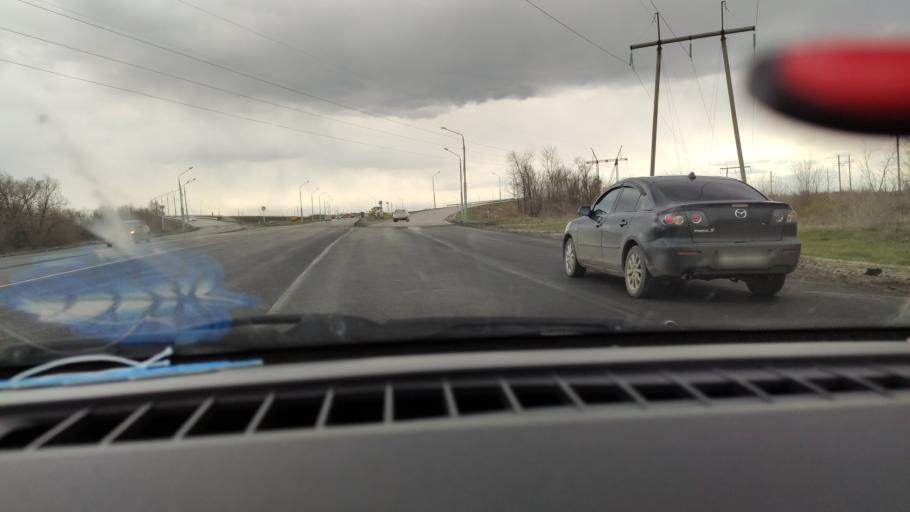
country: RU
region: Saratov
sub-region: Saratovskiy Rayon
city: Saratov
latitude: 51.6693
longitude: 45.9984
